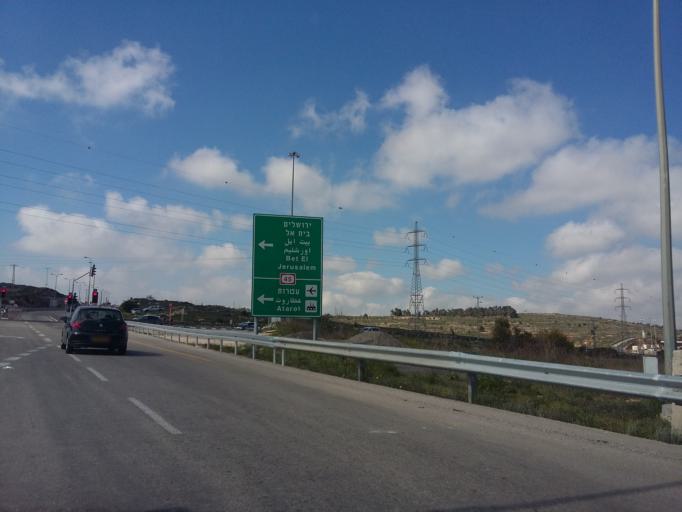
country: PS
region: West Bank
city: Rafat
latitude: 31.8713
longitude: 35.1783
